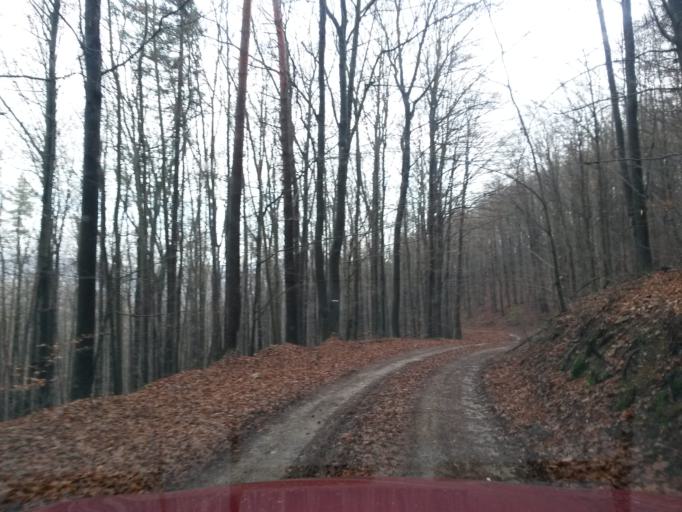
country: SK
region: Kosicky
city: Dobsina
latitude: 48.7485
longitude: 20.3990
